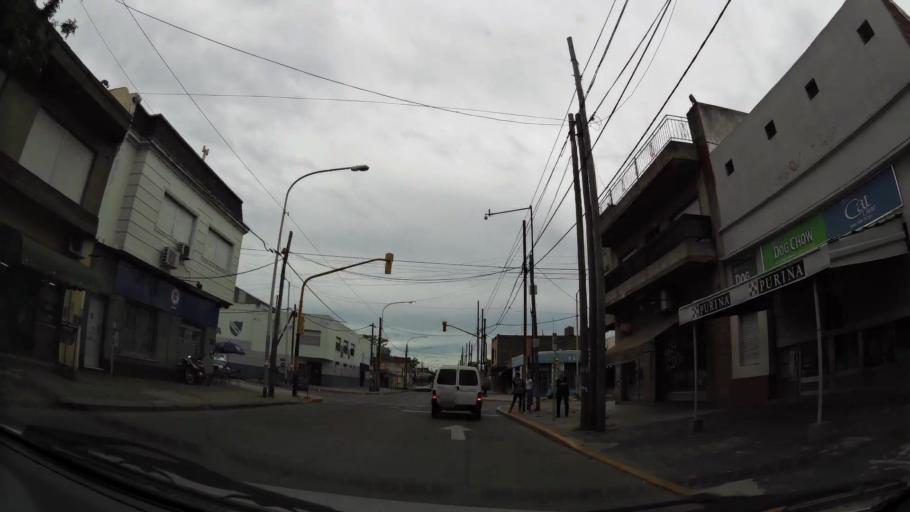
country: AR
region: Buenos Aires
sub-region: Partido de Avellaneda
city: Avellaneda
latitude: -34.6864
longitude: -58.3711
